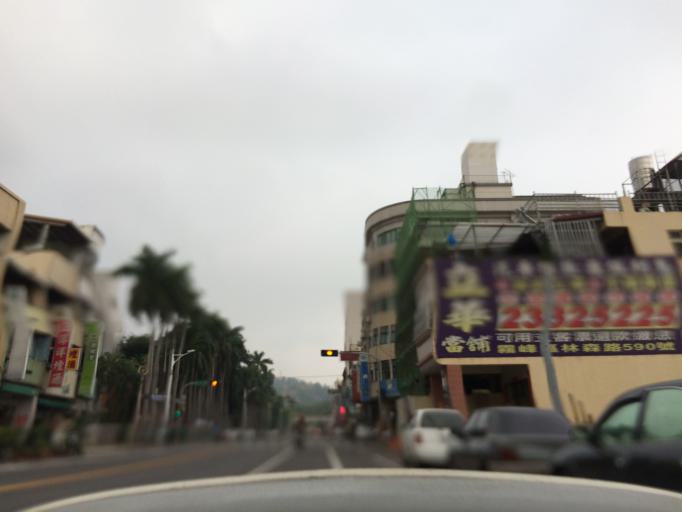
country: TW
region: Taiwan
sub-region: Taichung City
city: Taichung
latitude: 24.0600
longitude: 120.6980
